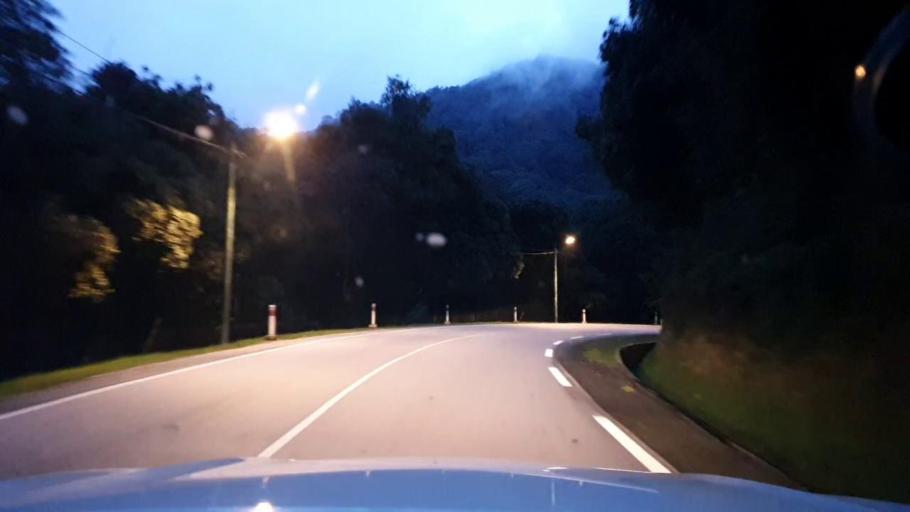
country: RW
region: Southern Province
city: Nzega
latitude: -2.5310
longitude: 29.3877
